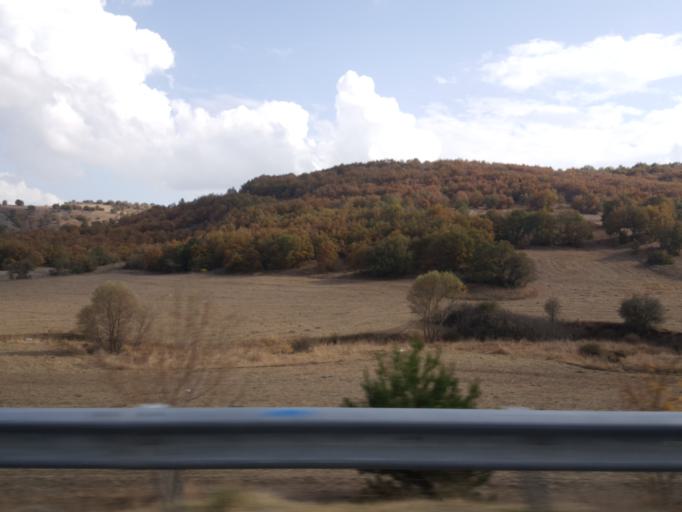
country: TR
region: Corum
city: Alaca
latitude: 40.3098
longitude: 34.6587
